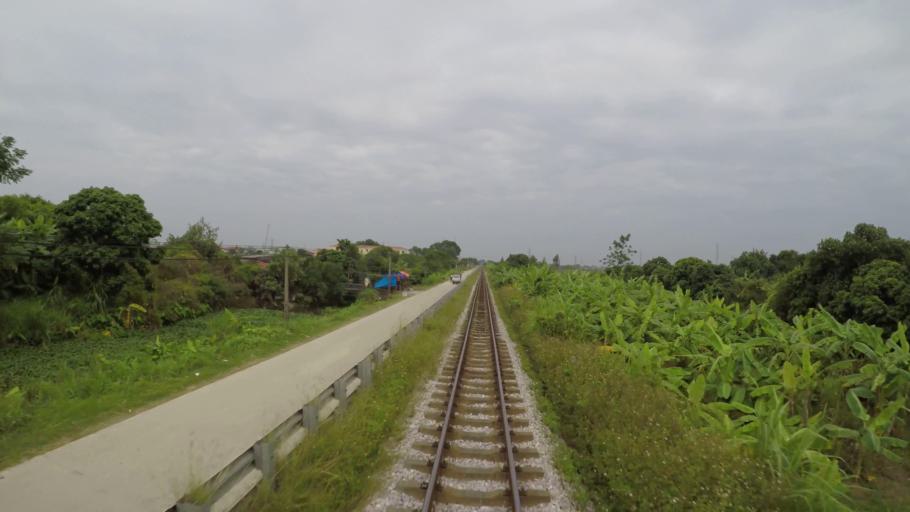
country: VN
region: Hai Duong
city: Lai Cach
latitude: 20.9509
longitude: 106.2395
